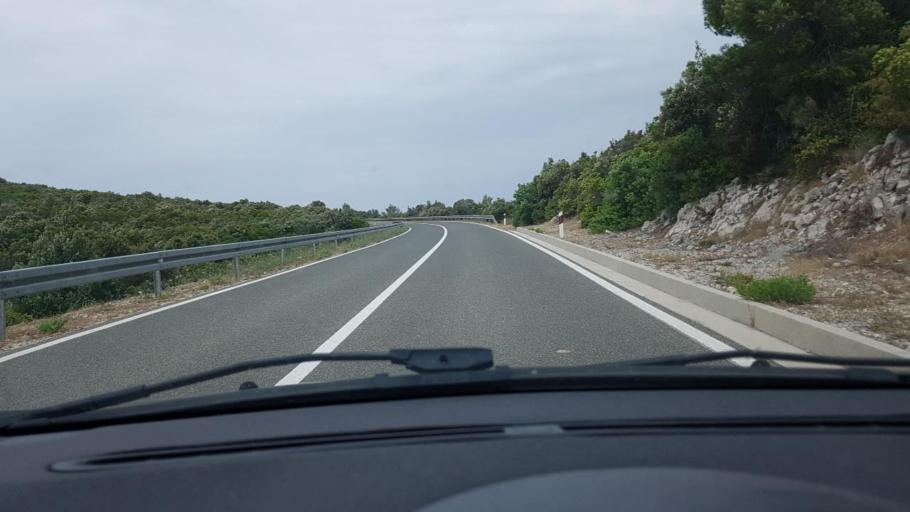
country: HR
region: Dubrovacko-Neretvanska
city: Smokvica
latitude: 42.9469
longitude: 16.9531
